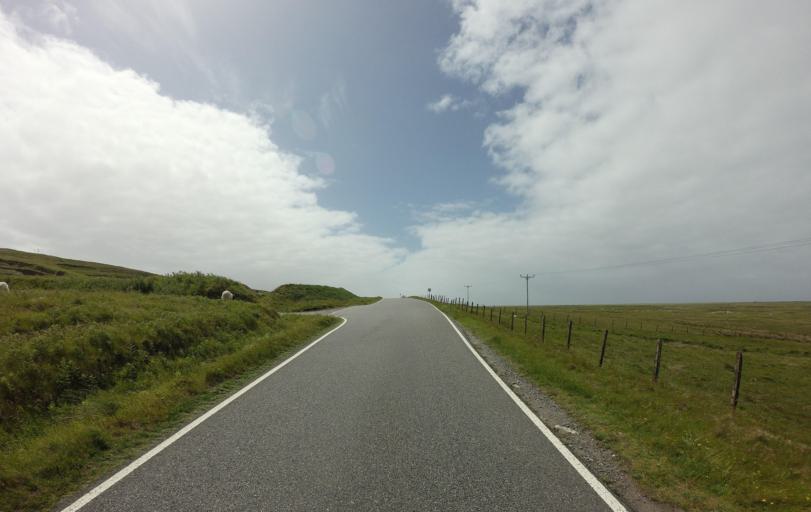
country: GB
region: Scotland
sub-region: Eilean Siar
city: Benbecula
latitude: 57.3464
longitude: -7.3620
